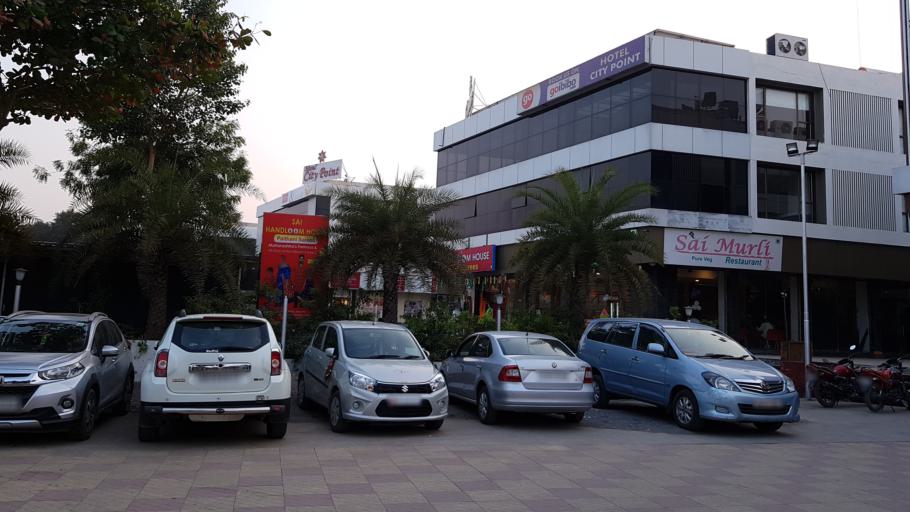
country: IN
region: Maharashtra
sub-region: Ahmadnagar
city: Shirdi
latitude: 19.7666
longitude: 74.4751
